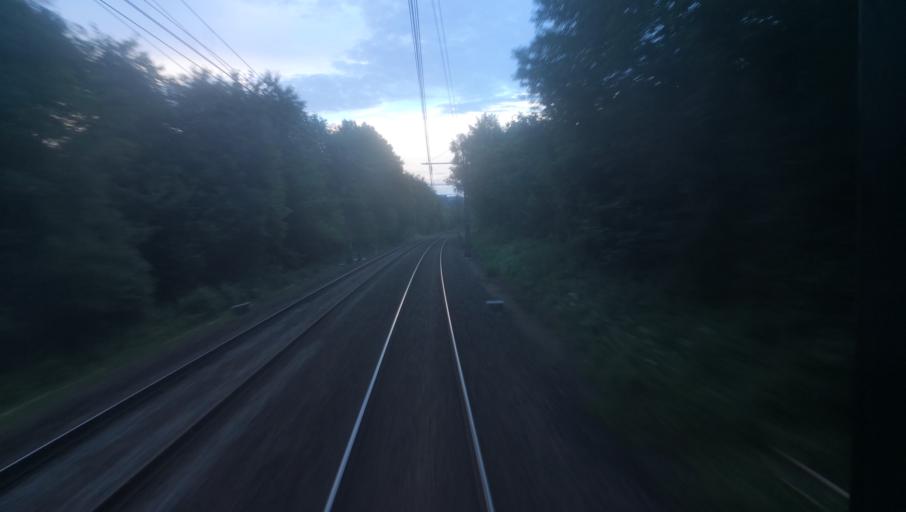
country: FR
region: Limousin
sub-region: Departement de la Haute-Vienne
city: Ambazac
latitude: 45.9884
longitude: 1.4718
